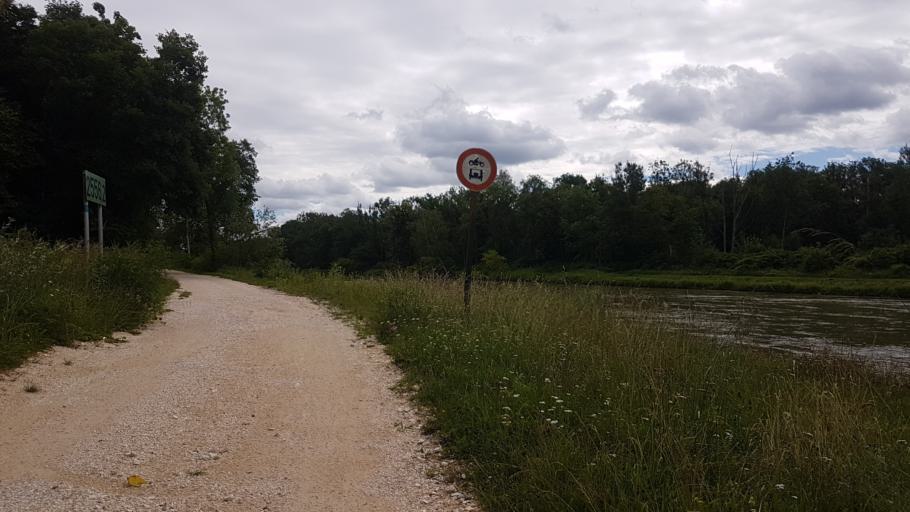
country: DE
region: Bavaria
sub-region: Swabia
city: Offingen
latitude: 48.4879
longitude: 10.3467
